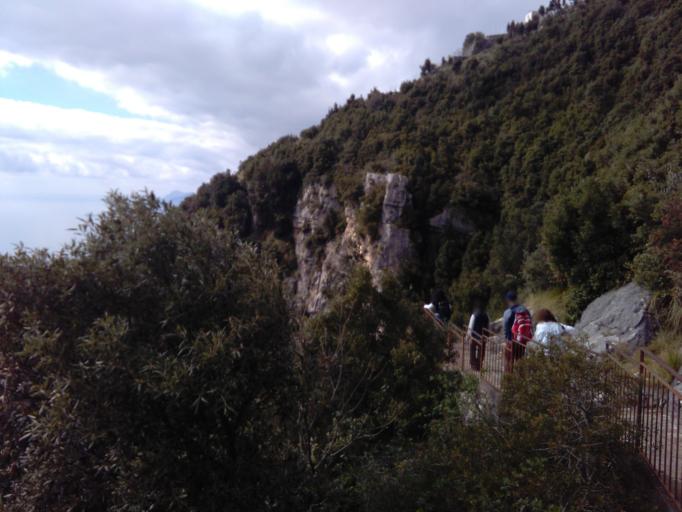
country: IT
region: Campania
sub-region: Provincia di Salerno
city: Praiano
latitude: 40.6299
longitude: 14.5086
